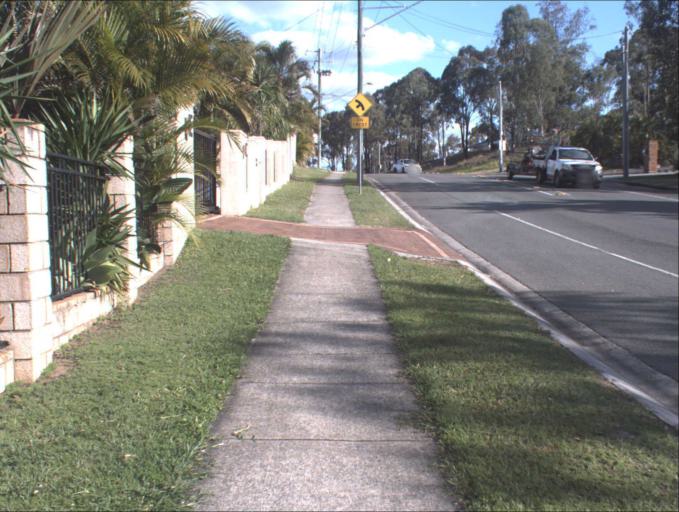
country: AU
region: Queensland
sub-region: Logan
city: Beenleigh
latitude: -27.7079
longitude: 153.1700
